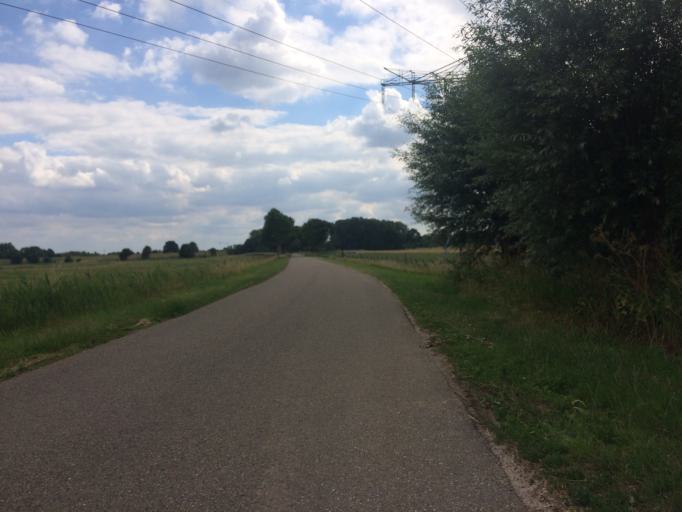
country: NL
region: Gelderland
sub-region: Gemeente Zaltbommel
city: Nederhemert-Noord
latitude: 51.7205
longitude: 5.2051
